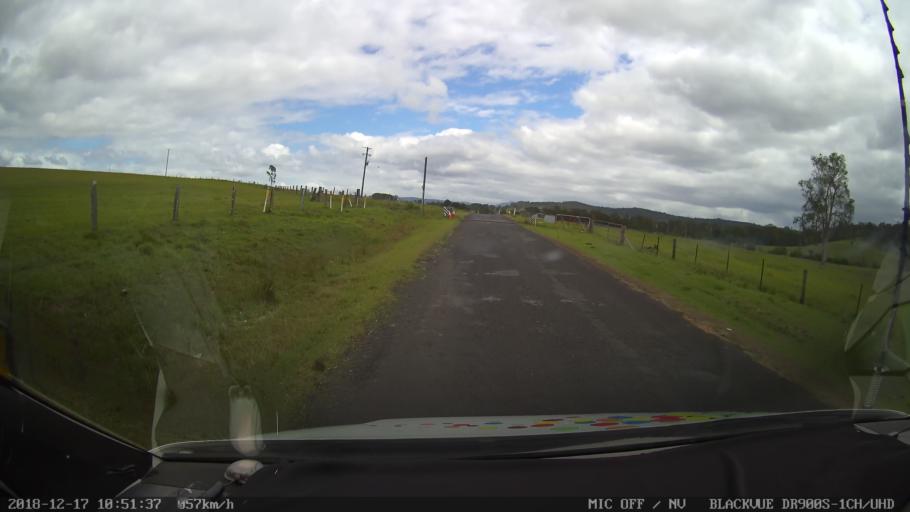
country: AU
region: New South Wales
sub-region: Tenterfield Municipality
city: Carrolls Creek
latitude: -28.8501
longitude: 152.5665
